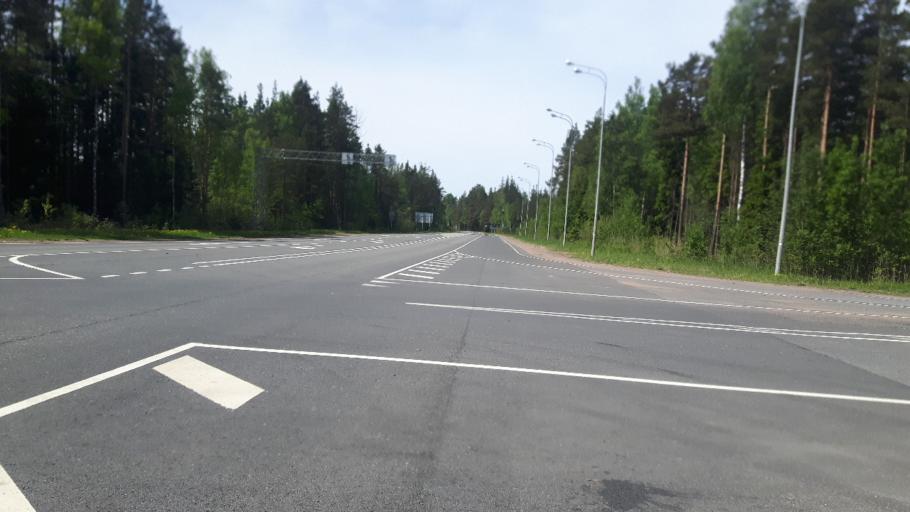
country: RU
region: Leningrad
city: Vistino
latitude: 59.6611
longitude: 28.4203
